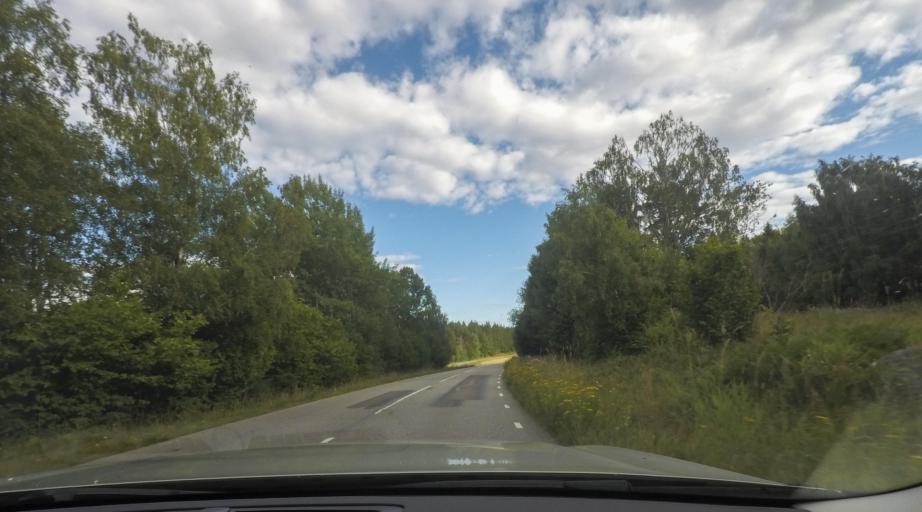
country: SE
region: Soedermanland
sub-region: Trosa Kommun
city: Trosa
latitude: 58.9795
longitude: 17.6903
